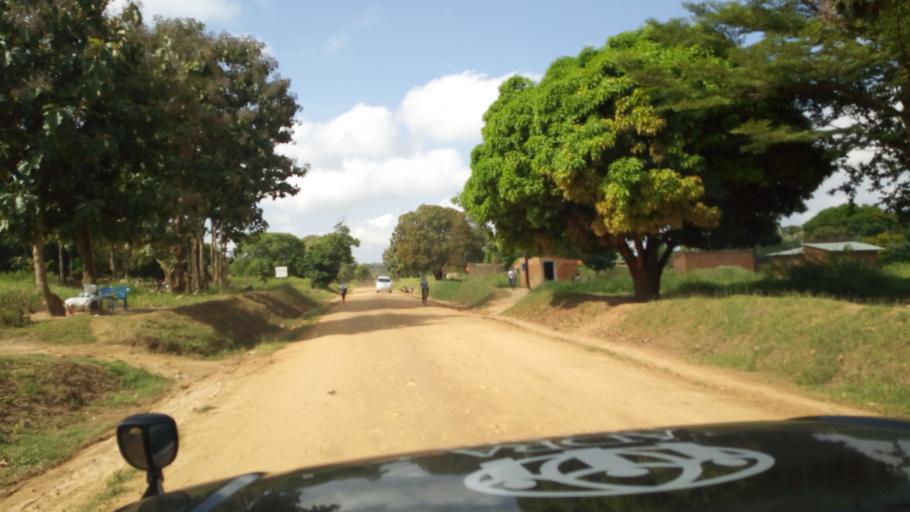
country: UG
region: Northern Region
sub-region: Moyo District
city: Moyo
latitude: 3.6519
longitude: 31.7090
